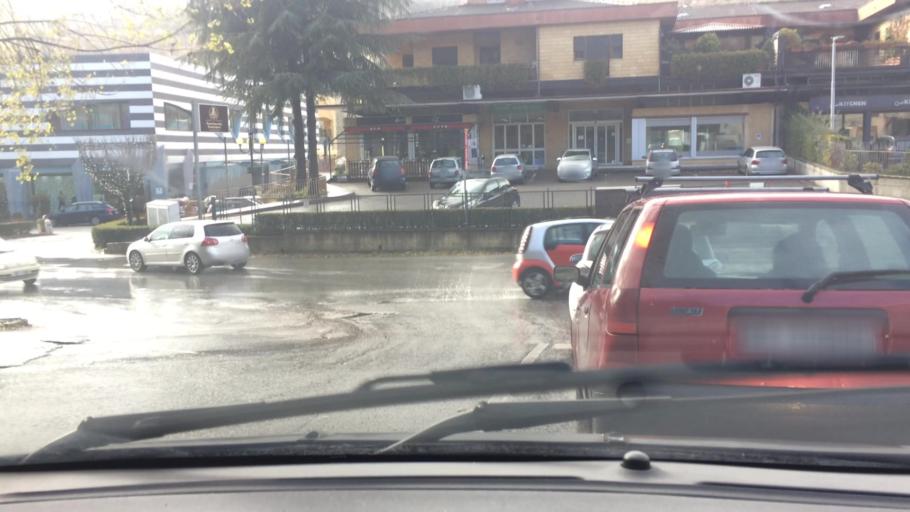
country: IT
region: Basilicate
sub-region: Provincia di Potenza
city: Potenza
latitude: 40.6334
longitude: 15.7885
